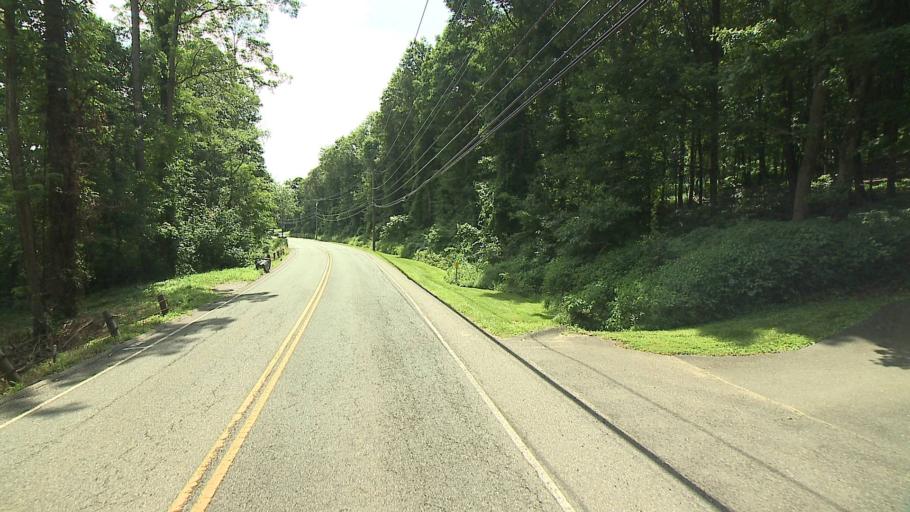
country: US
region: Connecticut
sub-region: Fairfield County
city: Sherman
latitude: 41.5554
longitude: -73.4886
